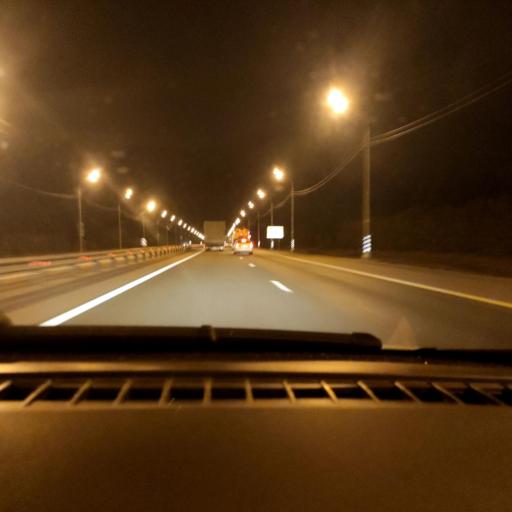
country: RU
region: Lipetsk
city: Khlevnoye
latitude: 52.2328
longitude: 39.0862
